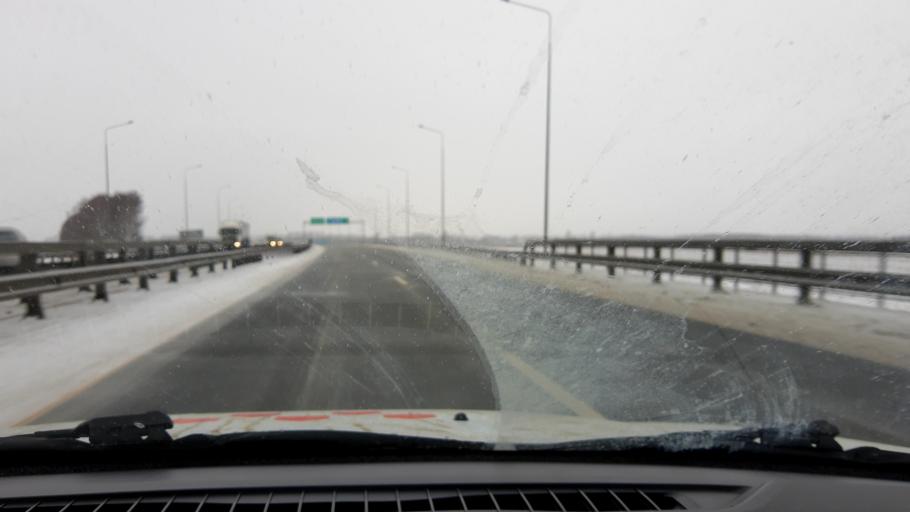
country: RU
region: Nizjnij Novgorod
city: Burevestnik
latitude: 56.1190
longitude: 43.9299
